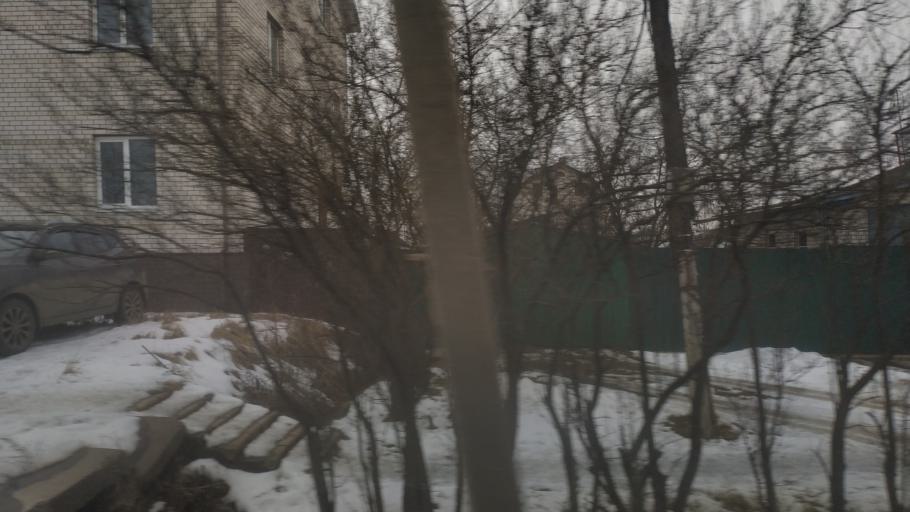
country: RU
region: Tverskaya
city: Tver
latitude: 56.8890
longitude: 35.8548
